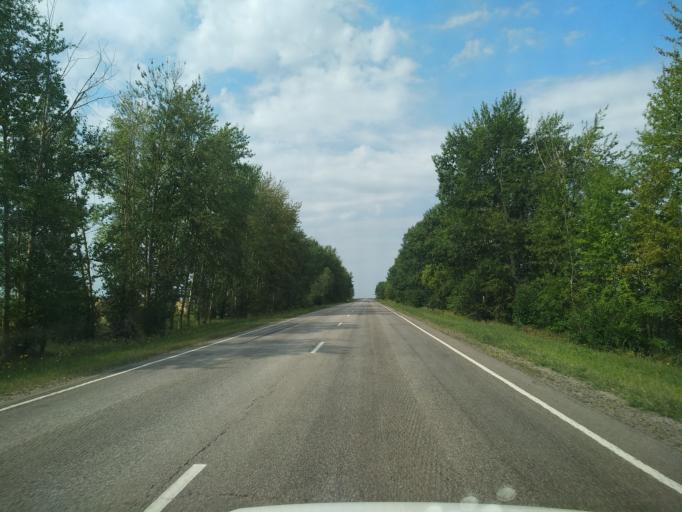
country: RU
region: Voronezj
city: Verkhnyaya Khava
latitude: 51.6961
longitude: 39.9544
